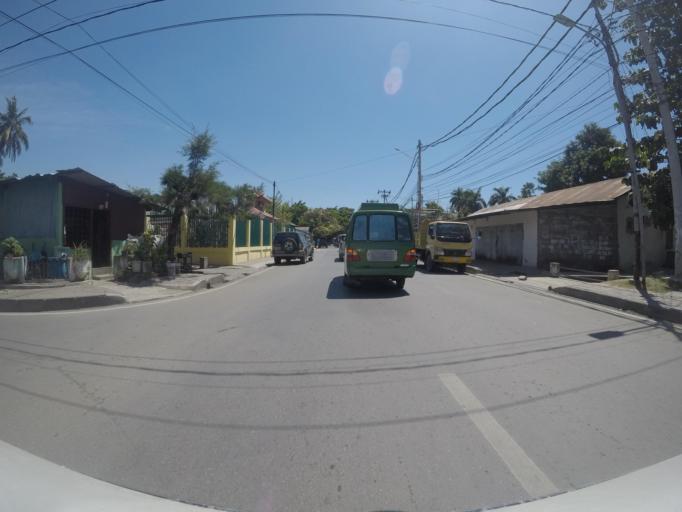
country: TL
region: Dili
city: Dili
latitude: -8.5551
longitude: 125.5810
